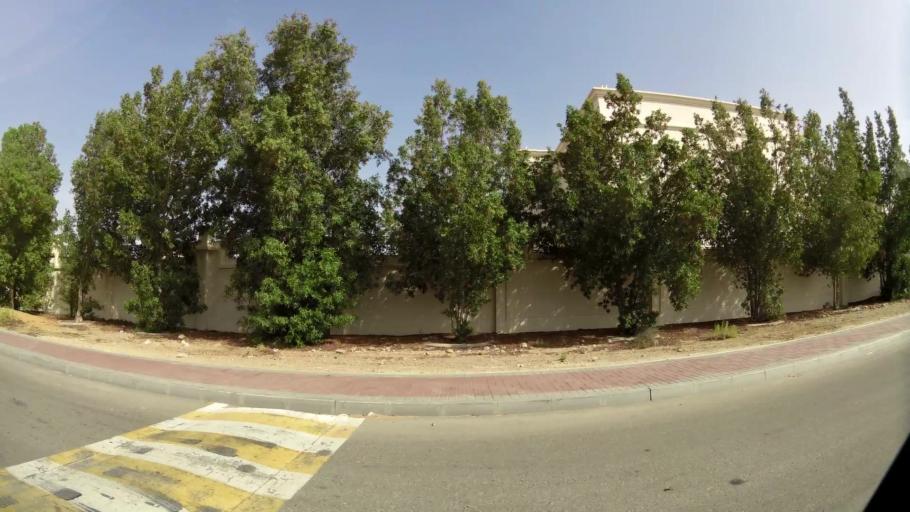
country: AE
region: Abu Dhabi
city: Al Ain
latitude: 24.2407
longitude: 55.6713
